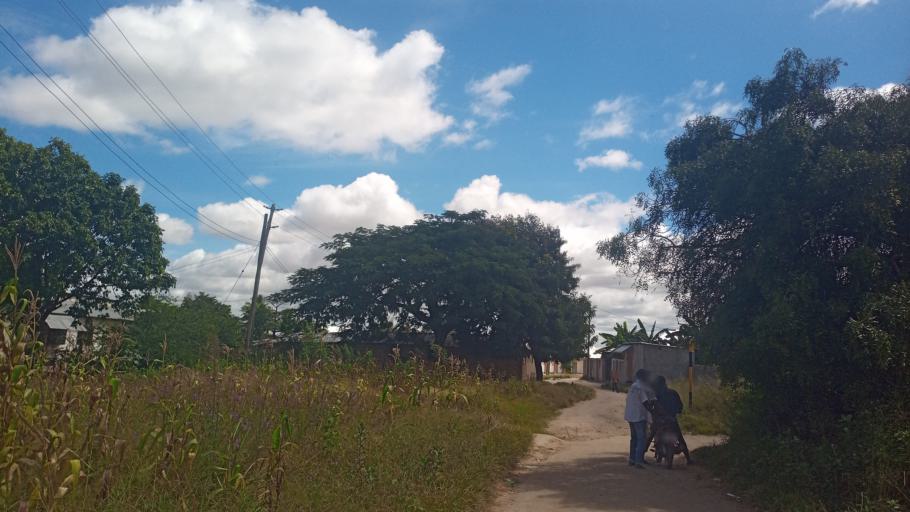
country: TZ
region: Dodoma
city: Dodoma
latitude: -6.1935
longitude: 35.7268
